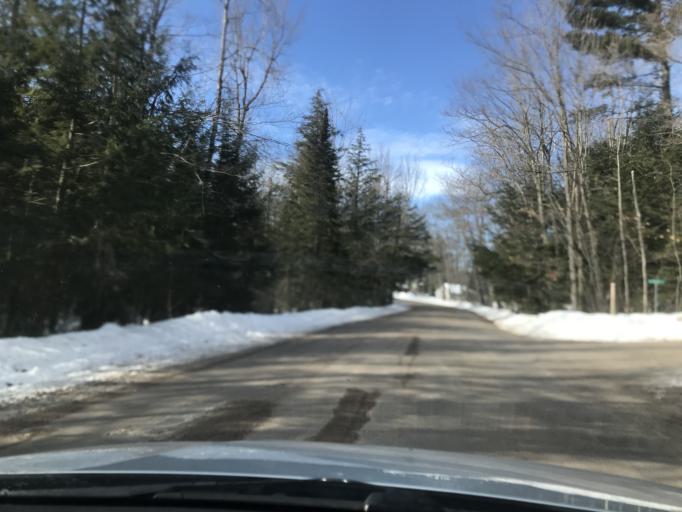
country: US
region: Wisconsin
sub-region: Menominee County
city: Legend Lake
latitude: 45.1189
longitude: -88.4306
